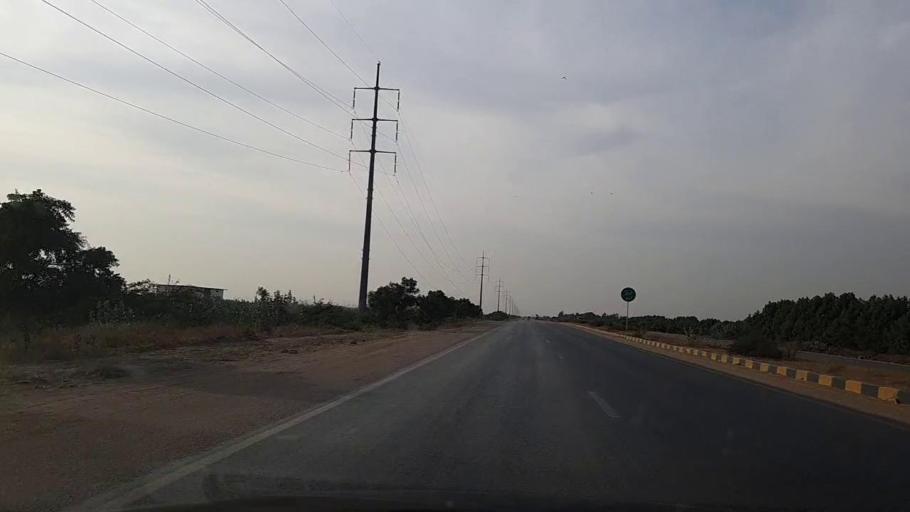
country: PK
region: Sindh
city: Gharo
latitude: 24.8211
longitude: 67.4826
